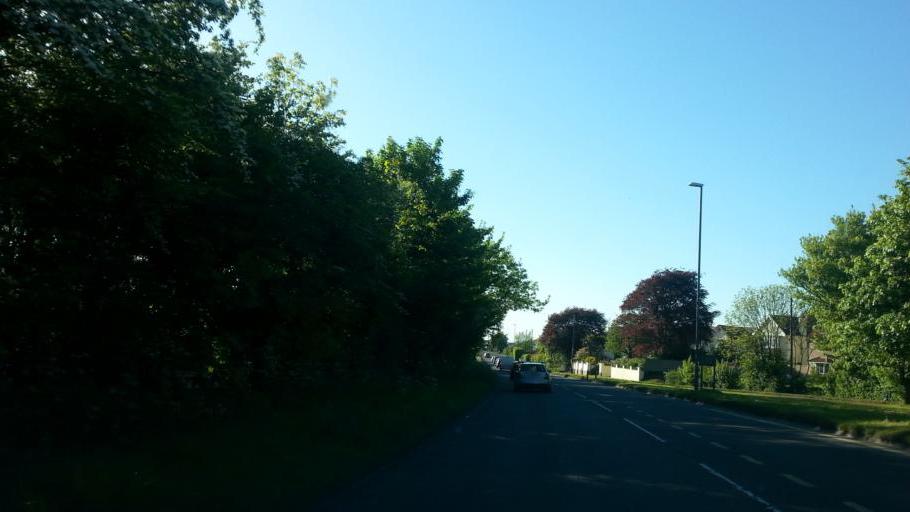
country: GB
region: England
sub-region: Bath and North East Somerset
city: Whitchurch
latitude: 51.4024
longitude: -2.5533
